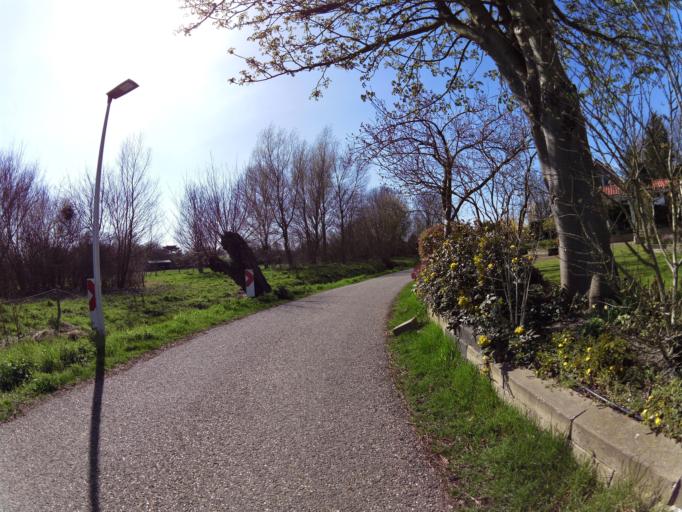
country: NL
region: South Holland
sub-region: Gemeente Brielle
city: Brielle
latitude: 51.9073
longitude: 4.1060
